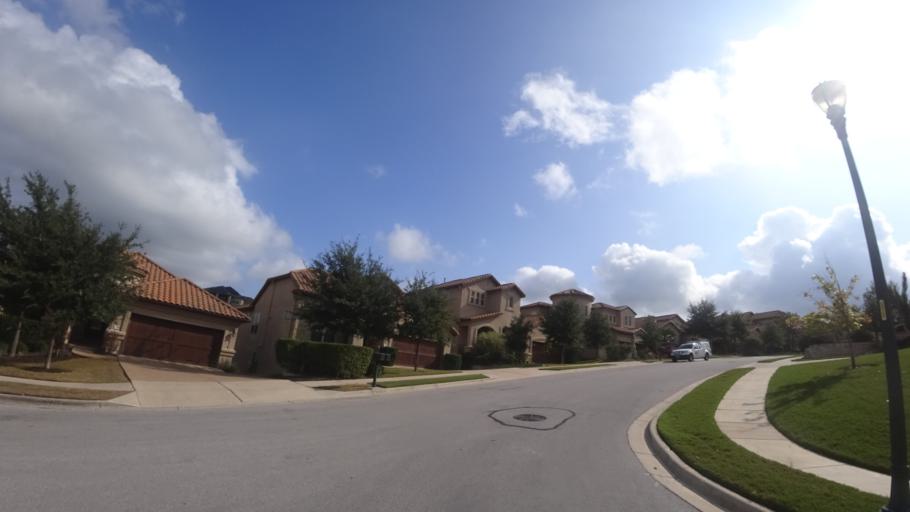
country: US
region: Texas
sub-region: Travis County
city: Bee Cave
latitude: 30.3126
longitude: -97.9036
